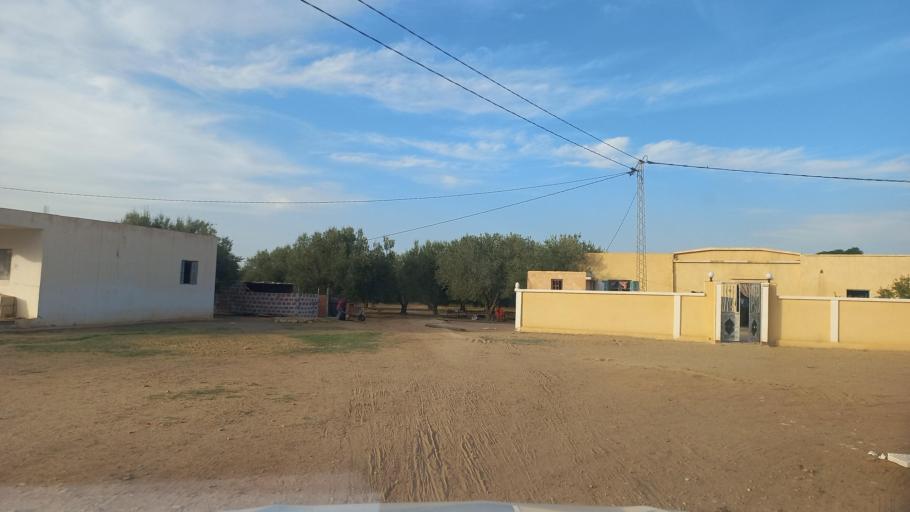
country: TN
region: Al Qasrayn
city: Kasserine
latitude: 35.2477
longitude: 9.0314
